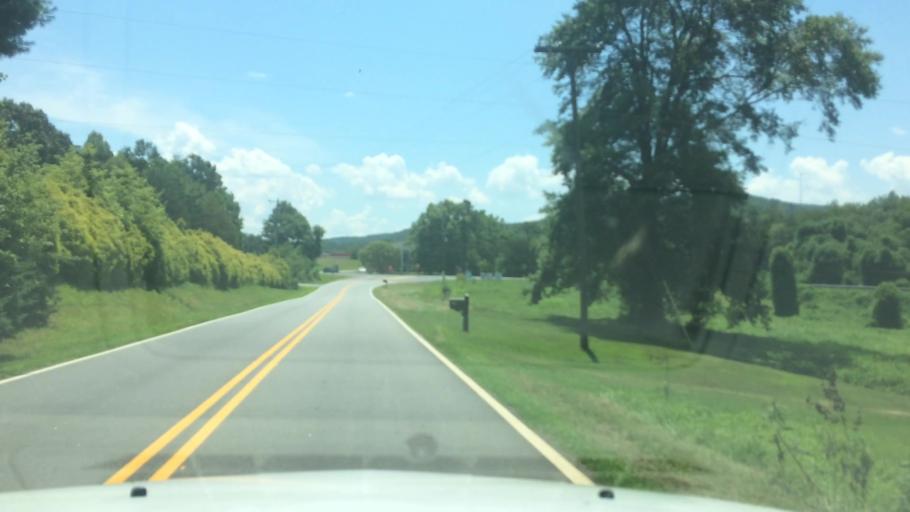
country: US
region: North Carolina
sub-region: Alexander County
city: Taylorsville
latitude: 35.9250
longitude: -81.2620
